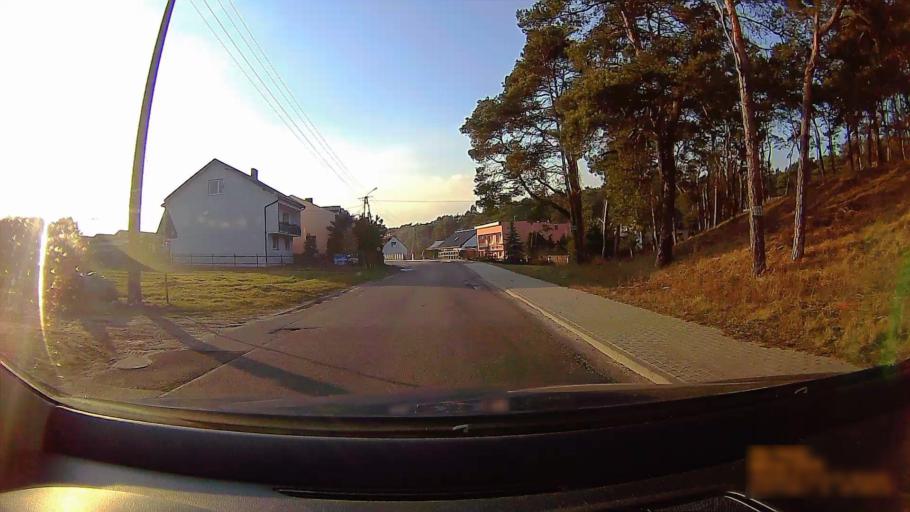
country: PL
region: Greater Poland Voivodeship
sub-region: Konin
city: Konin
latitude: 52.1970
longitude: 18.3128
